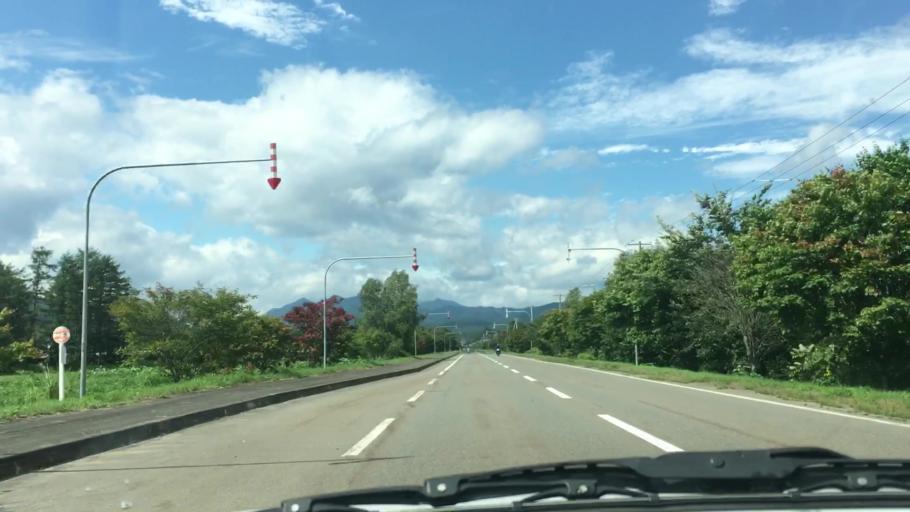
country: JP
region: Hokkaido
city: Otofuke
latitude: 43.3098
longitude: 143.3088
